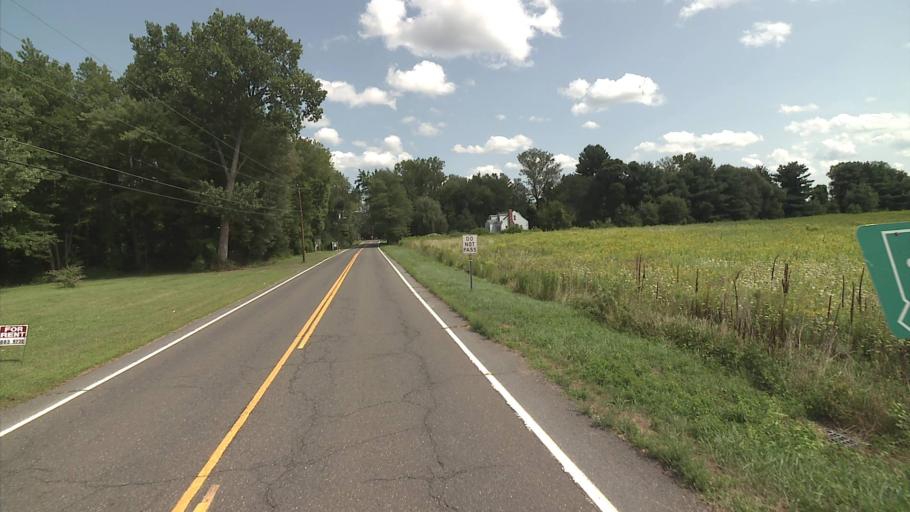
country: US
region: Connecticut
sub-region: Hartford County
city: Broad Brook
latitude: 41.8988
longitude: -72.5843
